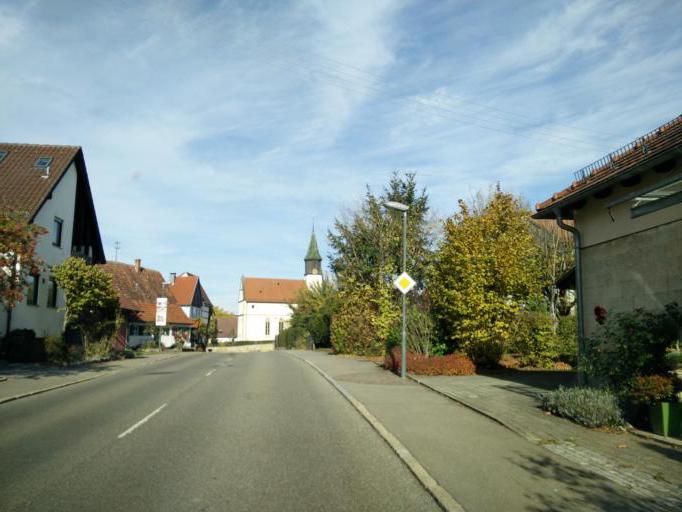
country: DE
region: Baden-Wuerttemberg
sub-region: Tuebingen Region
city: Gomaringen
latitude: 48.4780
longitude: 9.1027
